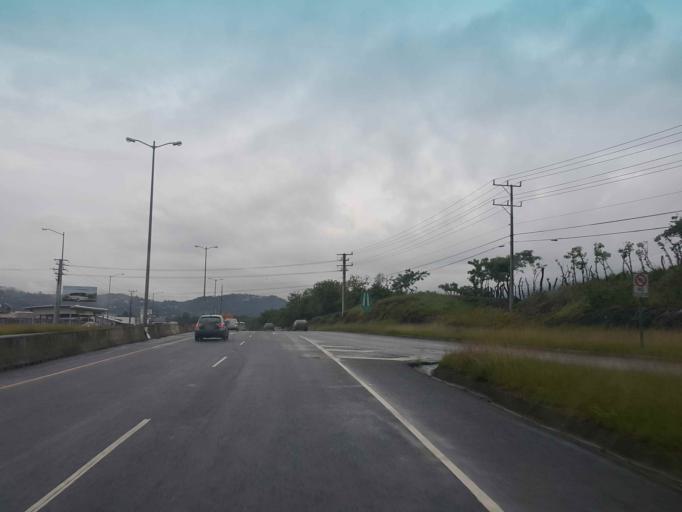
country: CR
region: Heredia
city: Colon
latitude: 9.9367
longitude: -84.2179
